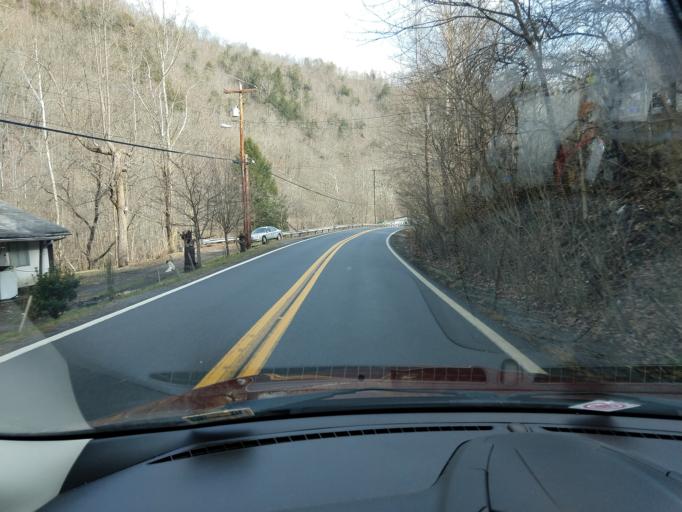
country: US
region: West Virginia
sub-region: McDowell County
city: Welch
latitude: 37.3423
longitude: -81.7529
